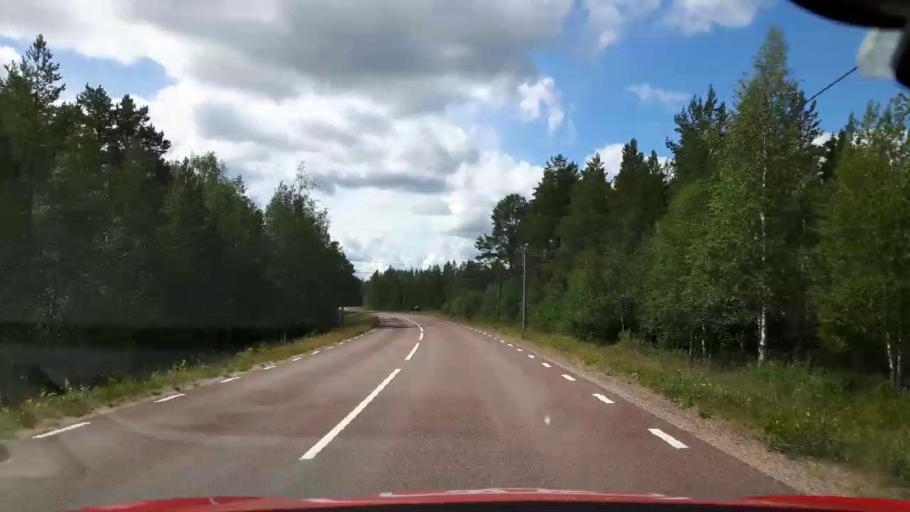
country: SE
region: Jaemtland
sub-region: Harjedalens Kommun
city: Sveg
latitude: 61.8632
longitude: 14.1118
